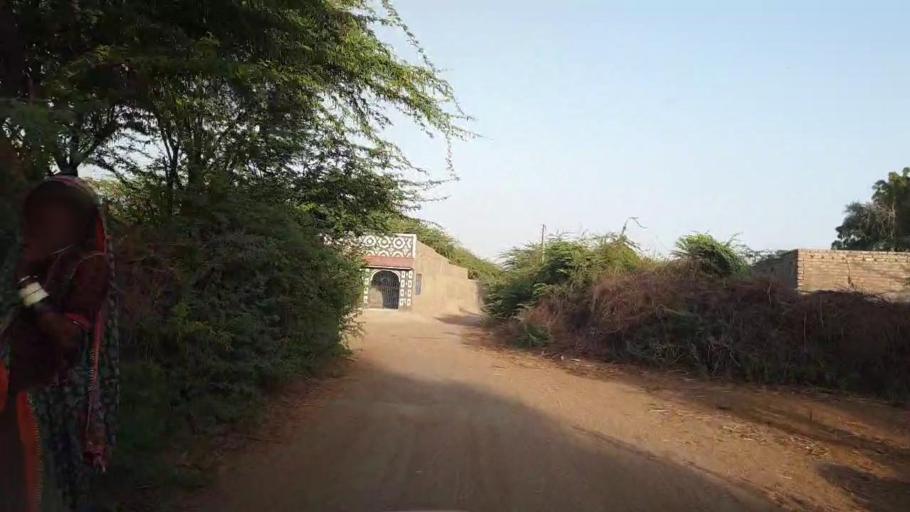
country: PK
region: Sindh
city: Tando Ghulam Ali
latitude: 25.1196
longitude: 68.9238
